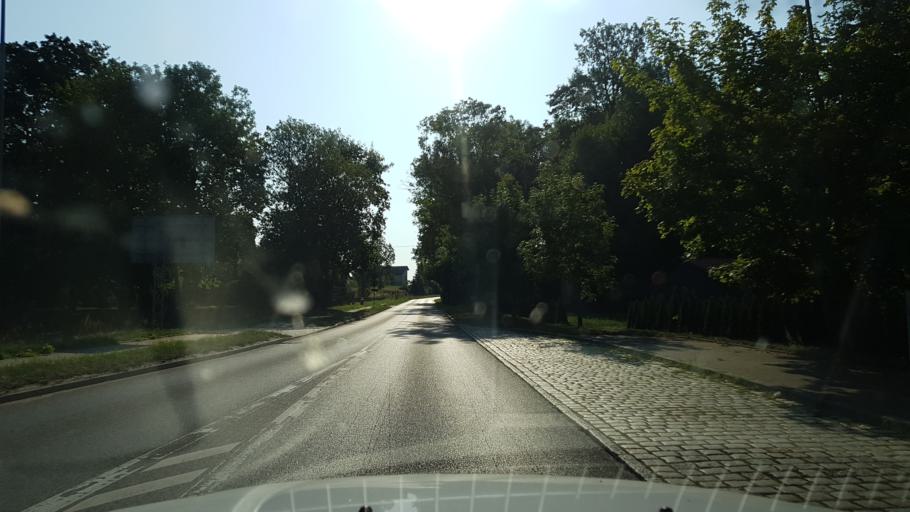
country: PL
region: West Pomeranian Voivodeship
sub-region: Powiat gryficki
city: Ploty
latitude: 53.7994
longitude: 15.2693
